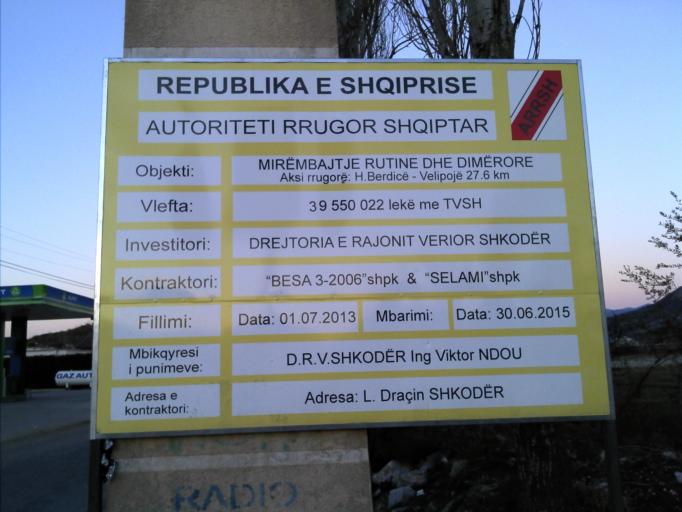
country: AL
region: Shkoder
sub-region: Rrethi i Malesia e Madhe
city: Kuc
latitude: 42.0319
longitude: 19.5028
